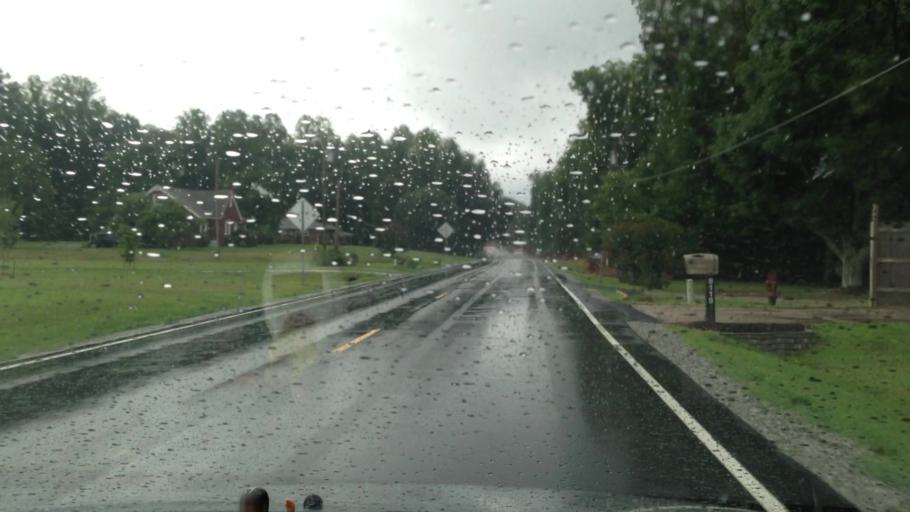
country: US
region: North Carolina
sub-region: Guilford County
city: Stokesdale
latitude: 36.2455
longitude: -79.9849
